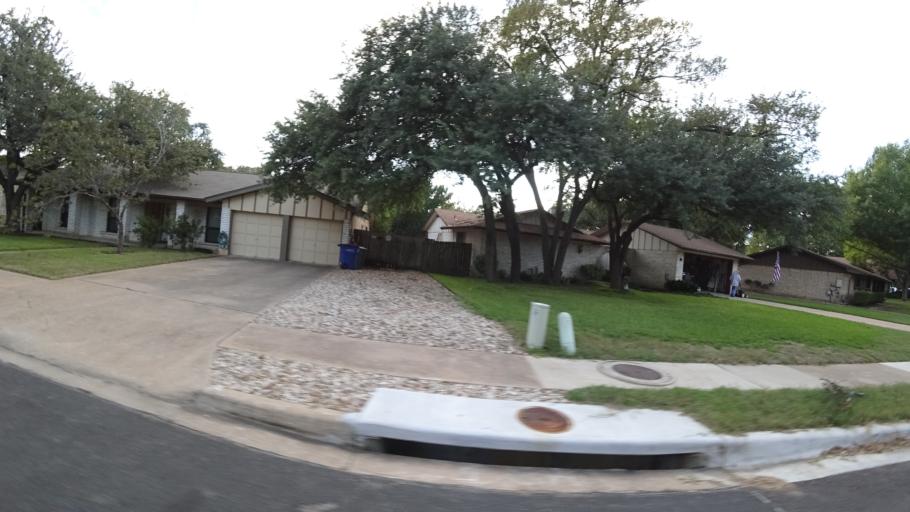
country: US
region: Texas
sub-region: Travis County
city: Austin
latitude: 30.2042
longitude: -97.7663
